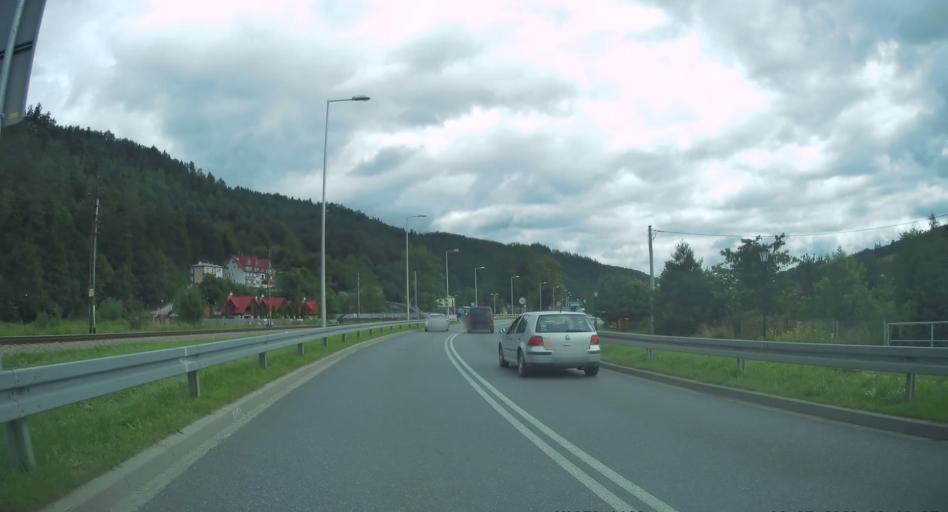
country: PL
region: Lesser Poland Voivodeship
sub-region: Powiat nowosadecki
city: Muszyna
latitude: 49.3566
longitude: 20.8949
